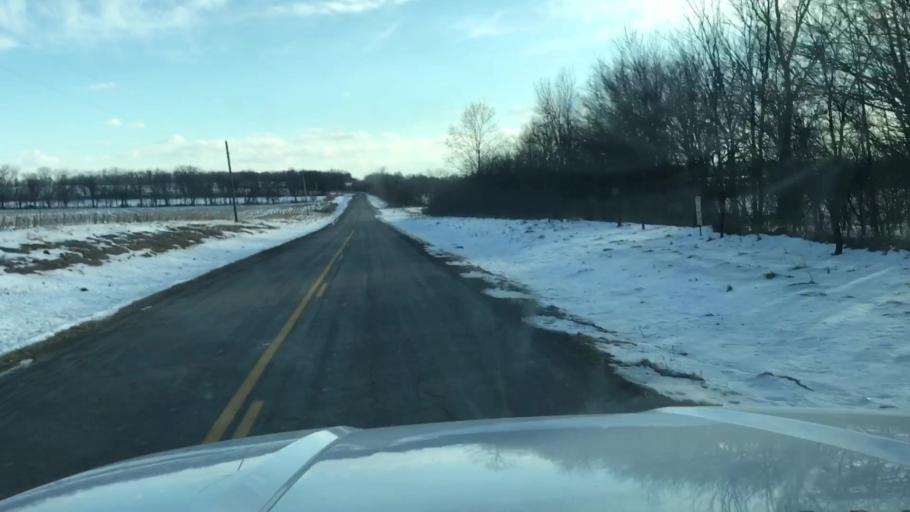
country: US
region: Missouri
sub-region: Holt County
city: Oregon
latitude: 40.1095
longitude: -95.0226
